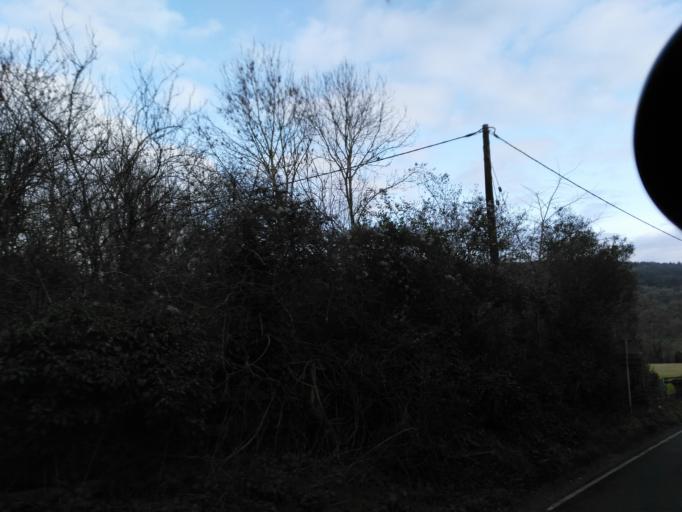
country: GB
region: England
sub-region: Bath and North East Somerset
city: Freshford
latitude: 51.3594
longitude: -2.3174
